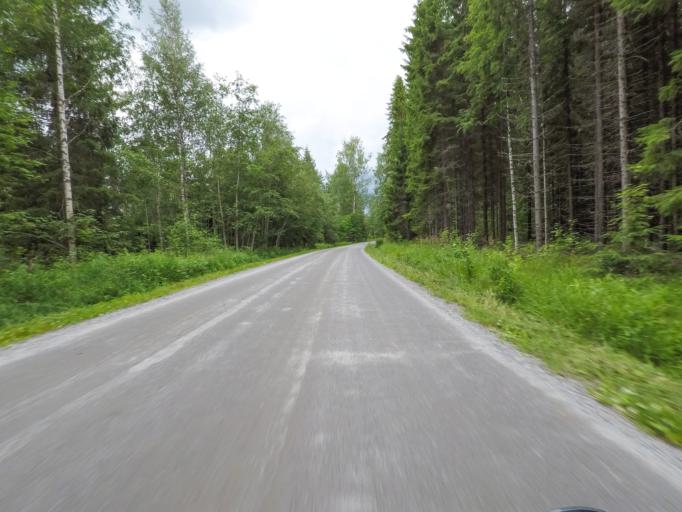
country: FI
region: Central Finland
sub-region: Jyvaeskylae
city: Hankasalmi
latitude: 62.4203
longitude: 26.6454
